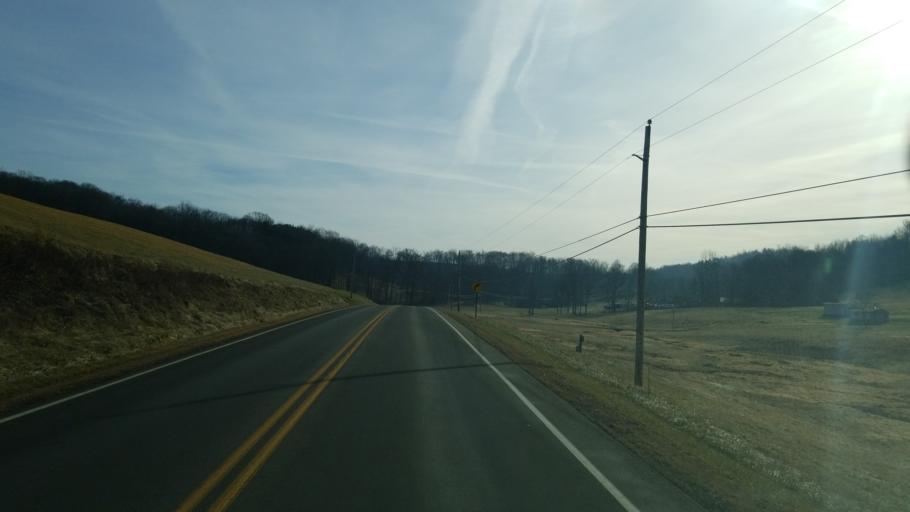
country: US
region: Pennsylvania
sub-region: Indiana County
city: Chevy Chase Heights
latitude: 40.7553
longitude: -79.1194
